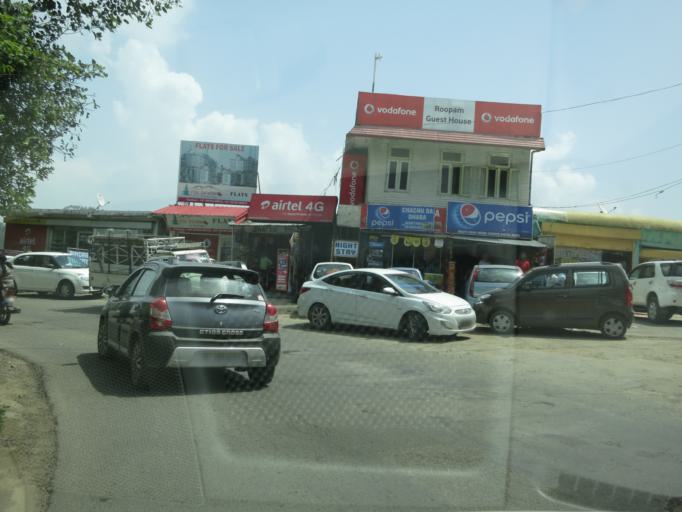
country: IN
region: Himachal Pradesh
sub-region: Solan
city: Dagshai
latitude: 30.8891
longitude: 77.0749
